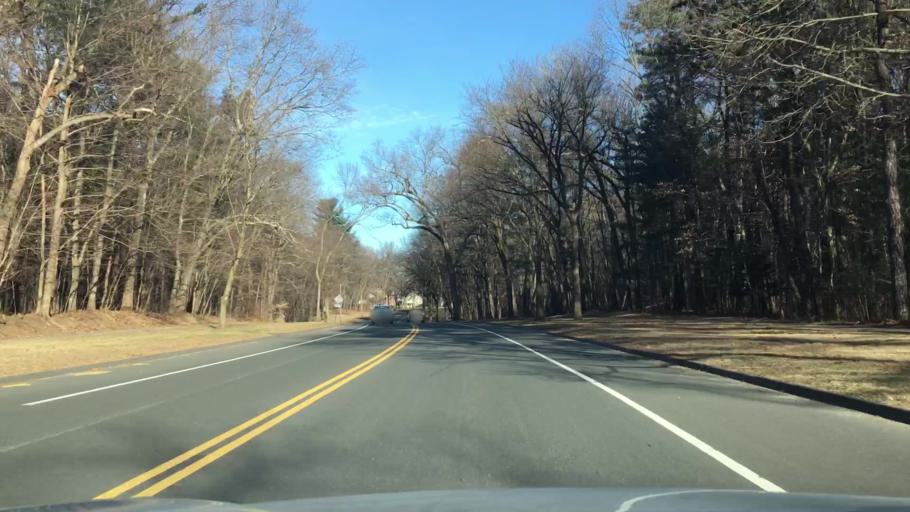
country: US
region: Massachusetts
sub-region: Hampden County
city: Longmeadow
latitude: 42.0587
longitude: -72.5722
